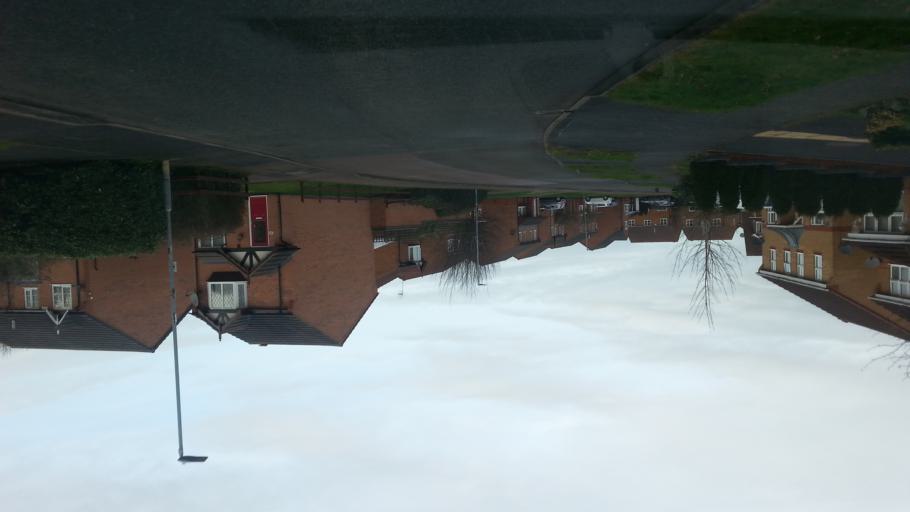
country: GB
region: England
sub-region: Leicestershire
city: Melton Mowbray
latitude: 52.7517
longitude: -0.8965
